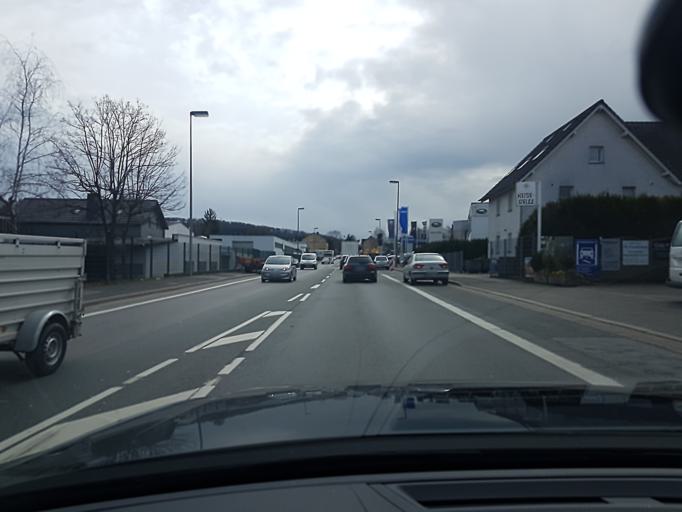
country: DE
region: North Rhine-Westphalia
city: Iserlohn
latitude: 51.4057
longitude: 7.6957
